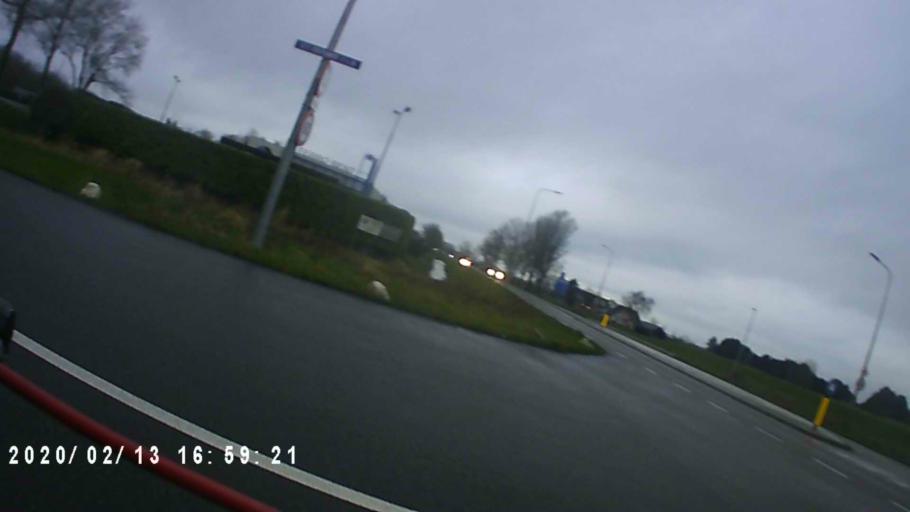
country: NL
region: Groningen
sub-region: Gemeente Groningen
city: Groningen
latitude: 53.2154
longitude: 6.5172
